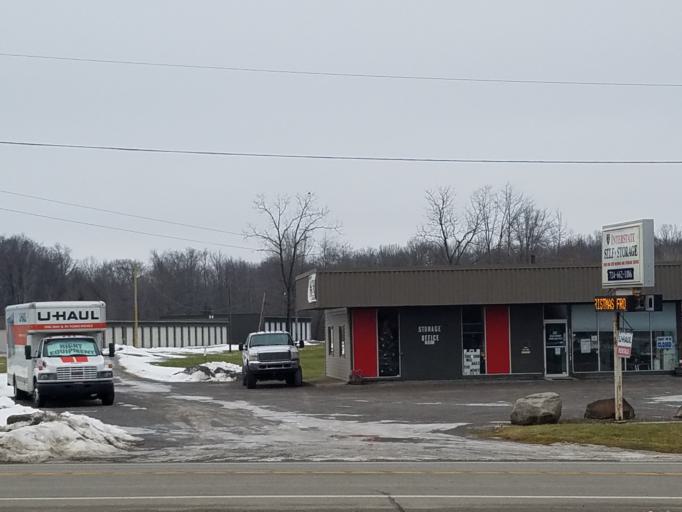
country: US
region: Pennsylvania
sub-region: Mercer County
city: Mercer
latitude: 41.2643
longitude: -80.1708
